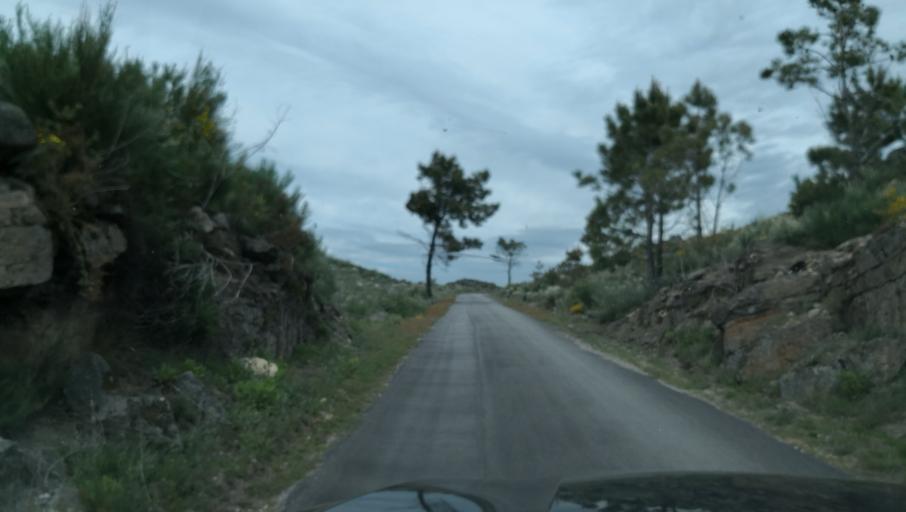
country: PT
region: Vila Real
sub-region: Vila Real
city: Vila Real
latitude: 41.3687
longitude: -7.6996
